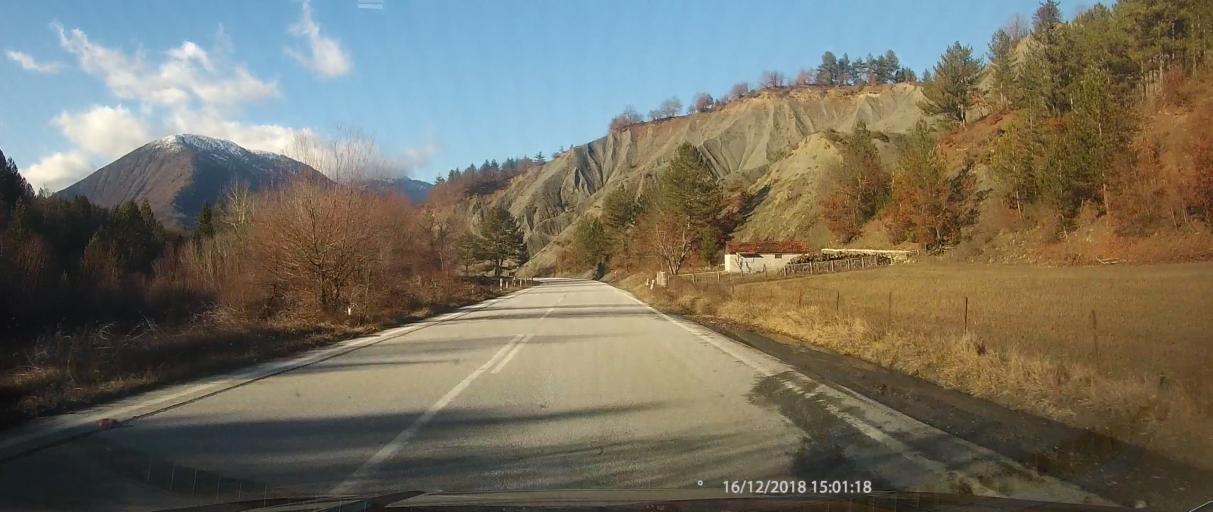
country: GR
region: West Macedonia
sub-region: Nomos Kastorias
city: Nestorio
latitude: 40.2204
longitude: 21.0074
